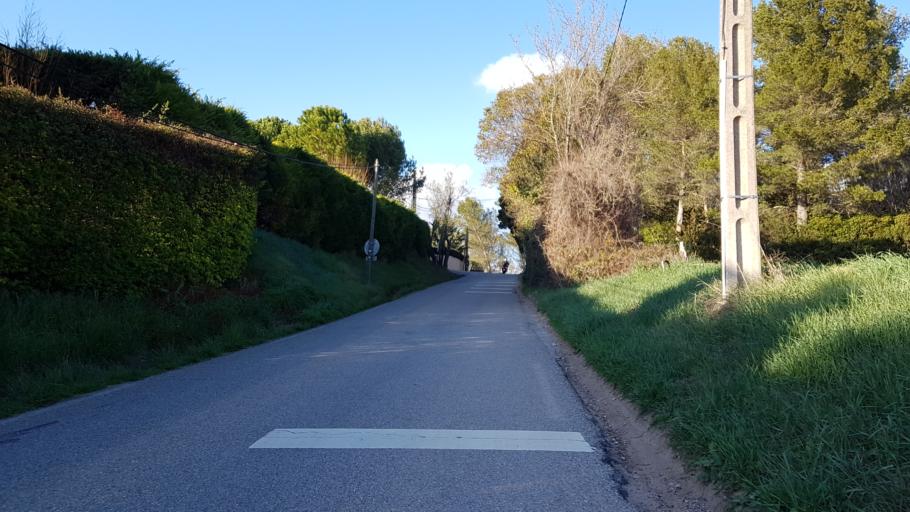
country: FR
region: Provence-Alpes-Cote d'Azur
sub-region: Departement des Bouches-du-Rhone
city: Bouc-Bel-Air
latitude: 43.4934
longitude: 5.3934
